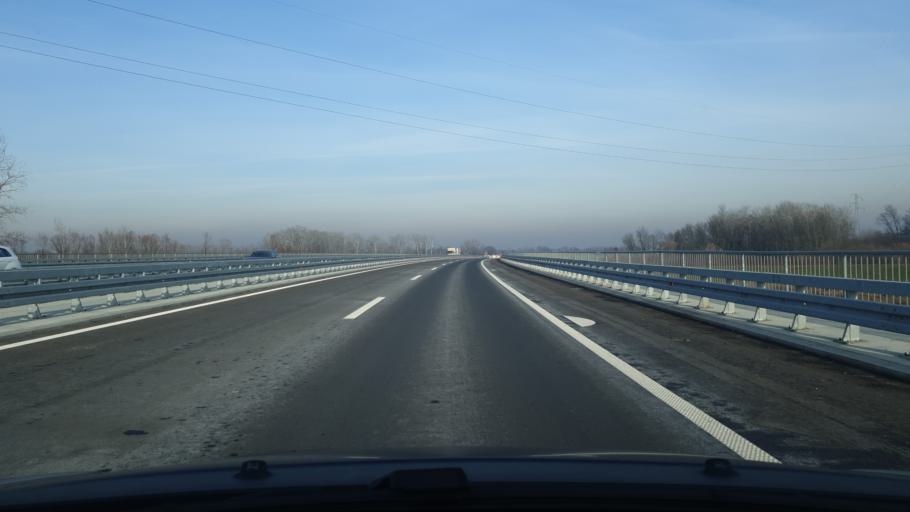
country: RS
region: Central Serbia
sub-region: Belgrade
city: Obrenovac
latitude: 44.6401
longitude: 20.2075
